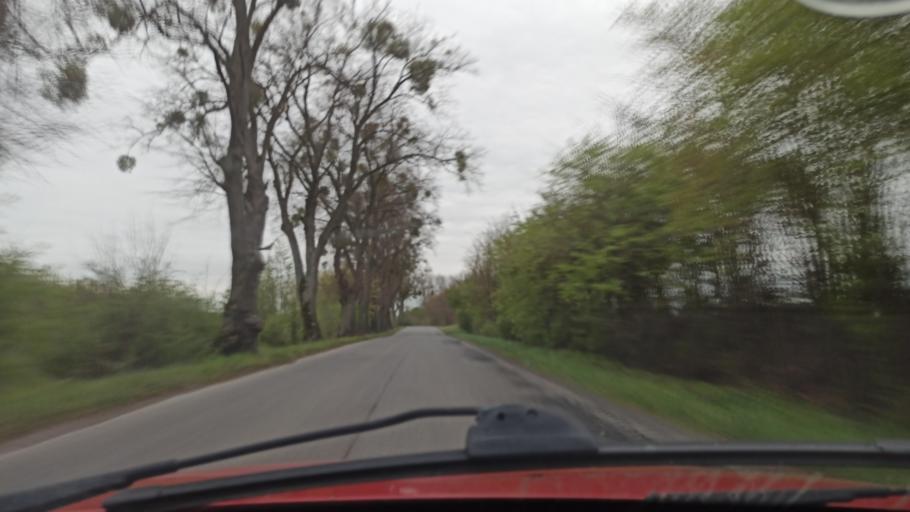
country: PL
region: Pomeranian Voivodeship
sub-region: Powiat kwidzynski
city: Gardeja
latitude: 53.5721
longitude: 18.9826
